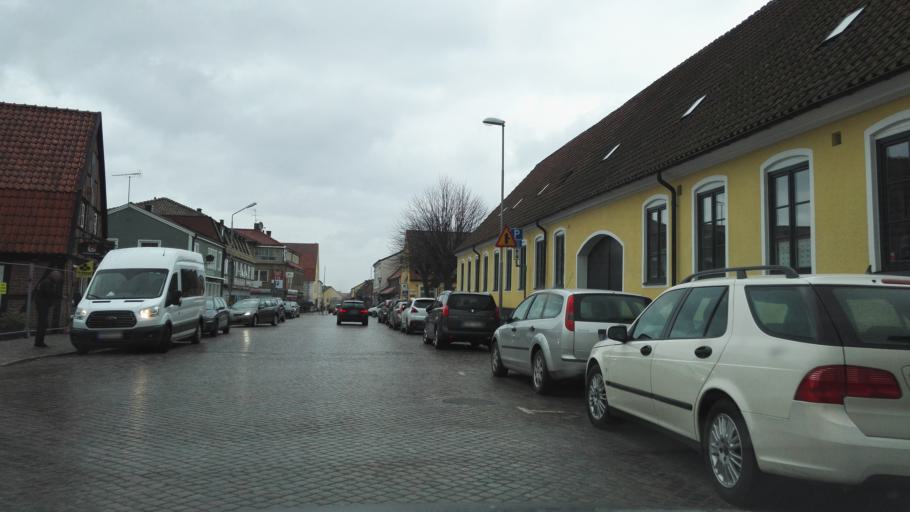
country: SE
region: Skane
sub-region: Simrishamns Kommun
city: Simrishamn
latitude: 55.5560
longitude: 14.3453
